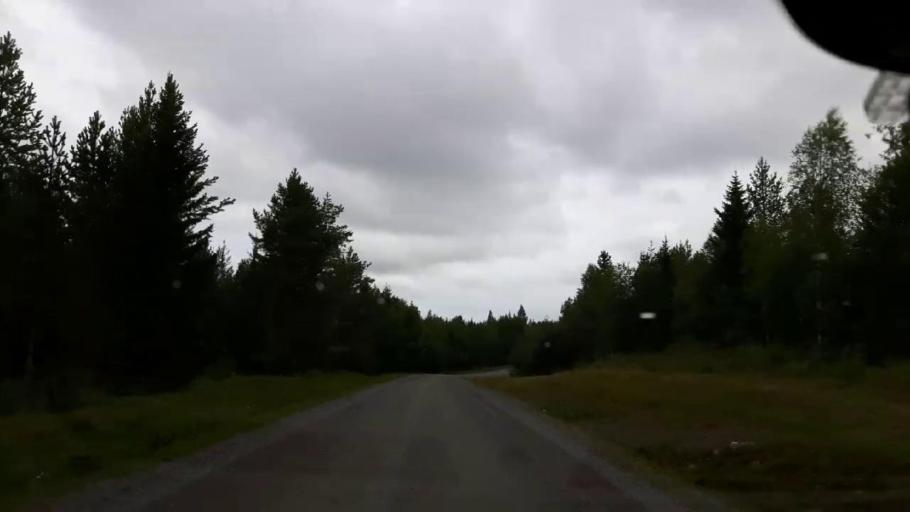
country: SE
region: Jaemtland
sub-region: OEstersunds Kommun
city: Ostersund
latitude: 63.0640
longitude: 14.5523
